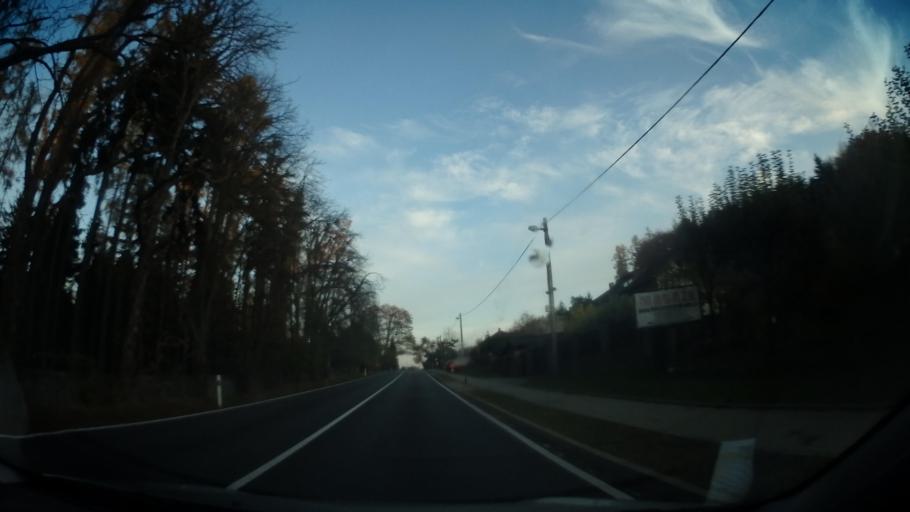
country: CZ
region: Central Bohemia
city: Vlasim
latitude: 49.6878
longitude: 14.9283
